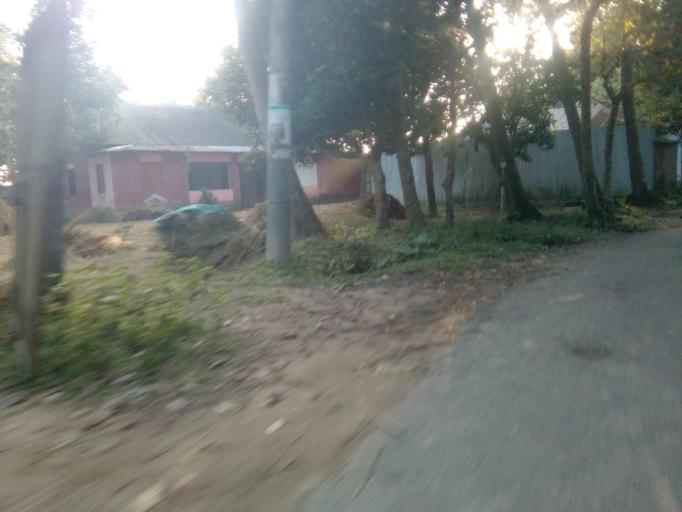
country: BD
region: Chittagong
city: Comilla
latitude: 23.4175
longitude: 91.2137
